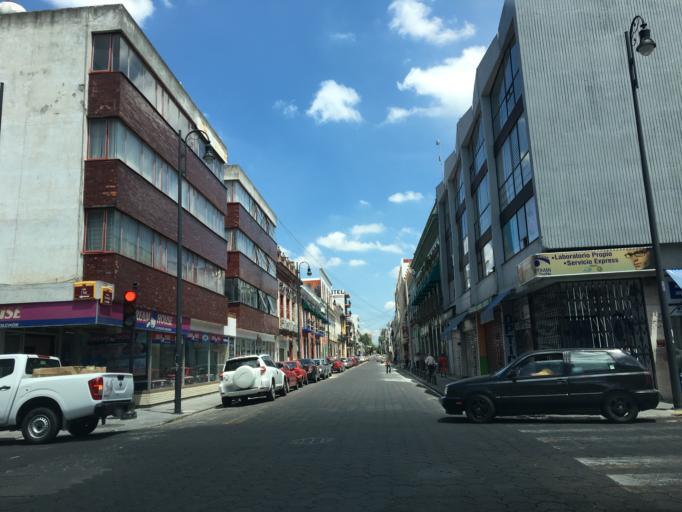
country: MX
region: Puebla
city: Puebla
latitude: 19.0460
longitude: -98.2036
